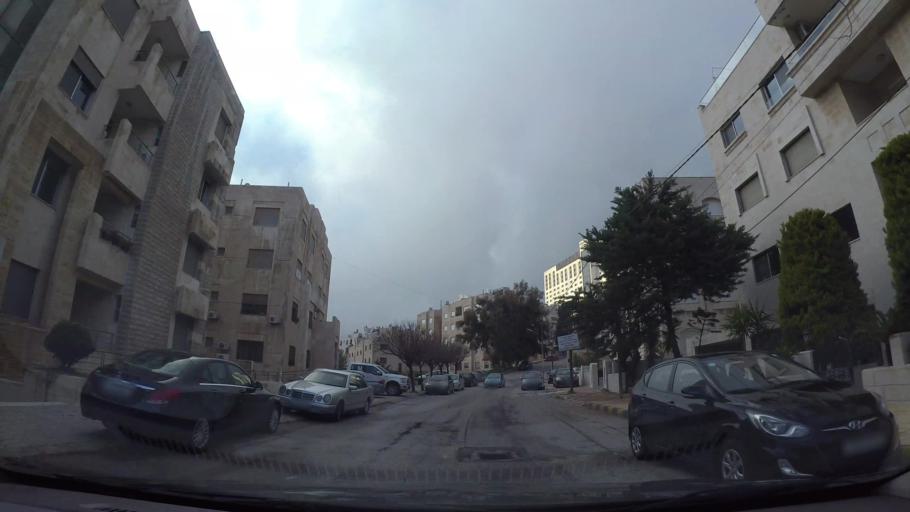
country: JO
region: Amman
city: Amman
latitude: 31.9575
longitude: 35.8827
